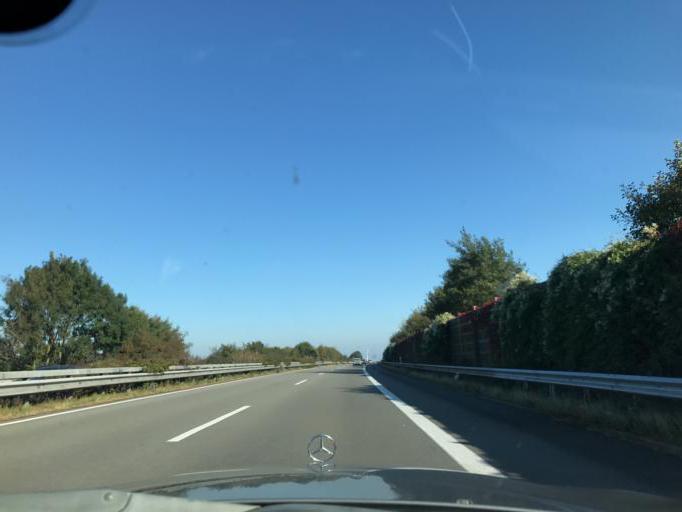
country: DE
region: Lower Saxony
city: Weener
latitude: 53.2111
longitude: 7.3193
